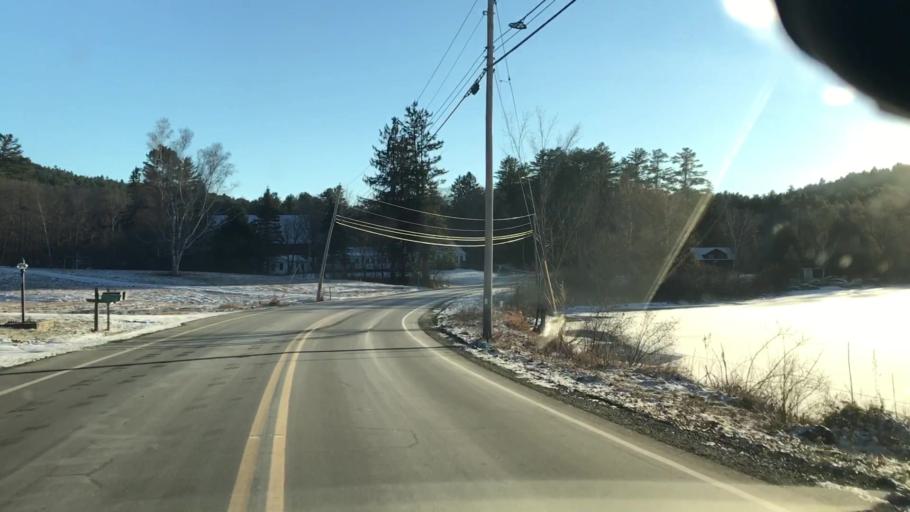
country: US
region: New Hampshire
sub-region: Grafton County
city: Lyme Town Offices
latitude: 43.8270
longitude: -72.1444
